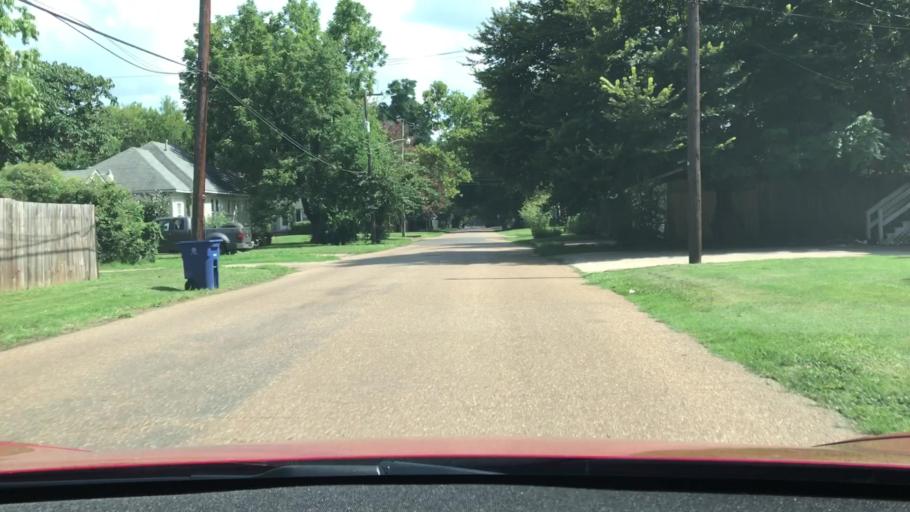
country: US
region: Louisiana
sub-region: Bossier Parish
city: Bossier City
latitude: 32.4752
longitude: -93.7313
